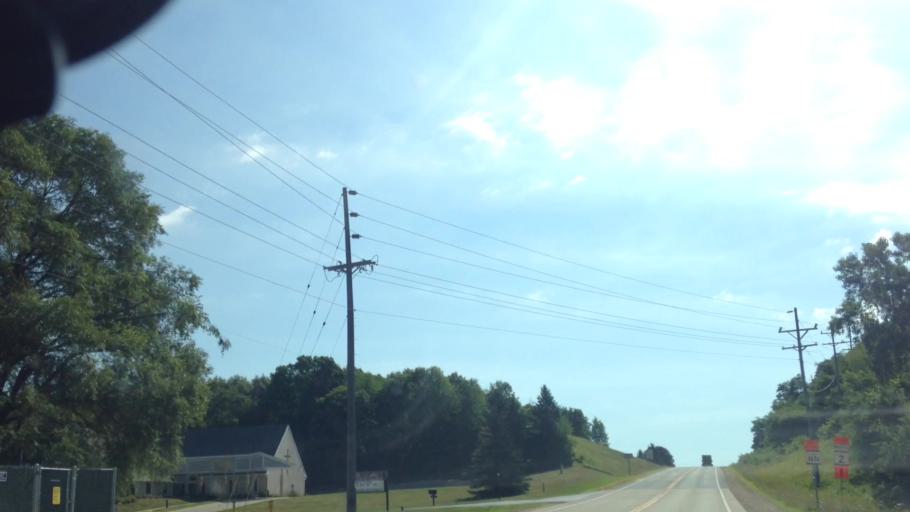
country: US
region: Wisconsin
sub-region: Washington County
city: Slinger
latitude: 43.3535
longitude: -88.2803
